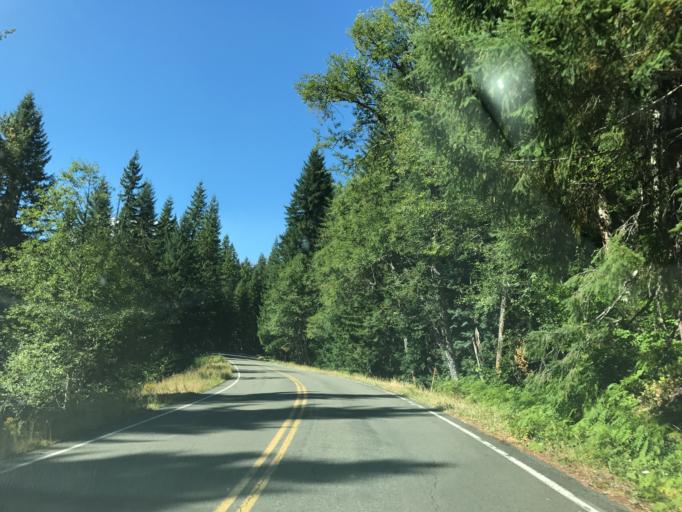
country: US
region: Washington
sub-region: Pierce County
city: Buckley
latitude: 46.7627
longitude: -121.6308
